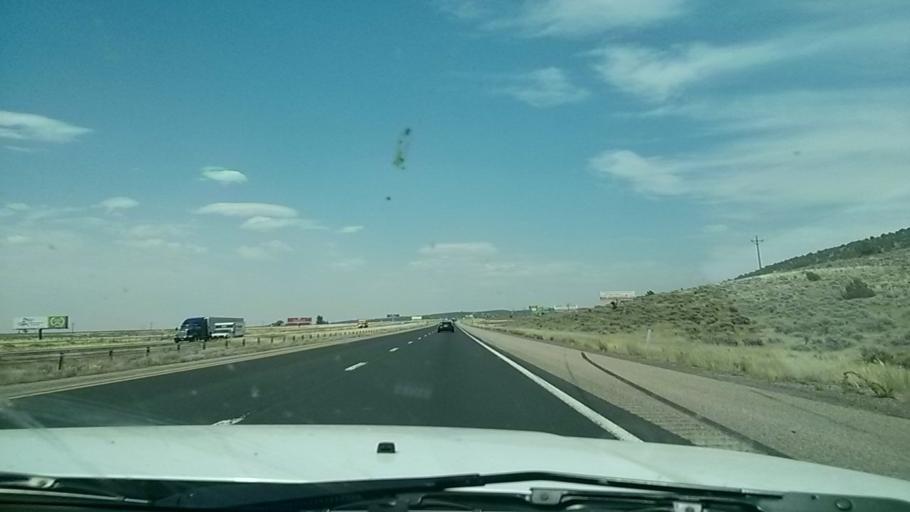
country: US
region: Utah
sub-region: Iron County
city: Cedar City
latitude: 37.6076
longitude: -113.1574
